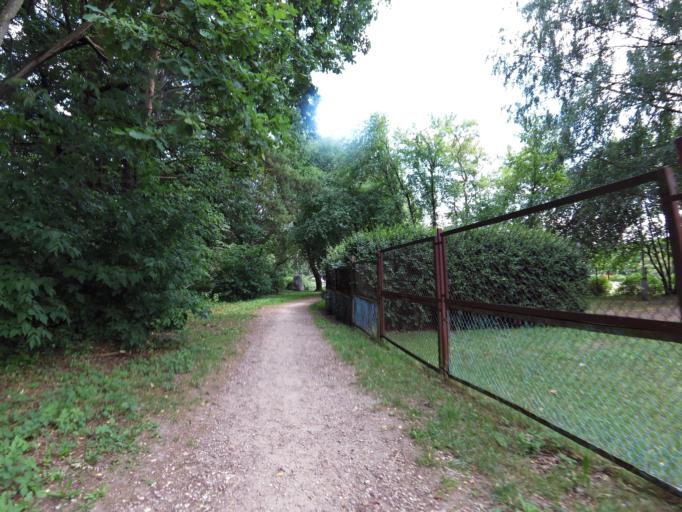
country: LT
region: Vilnius County
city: Lazdynai
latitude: 54.6850
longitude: 25.2176
